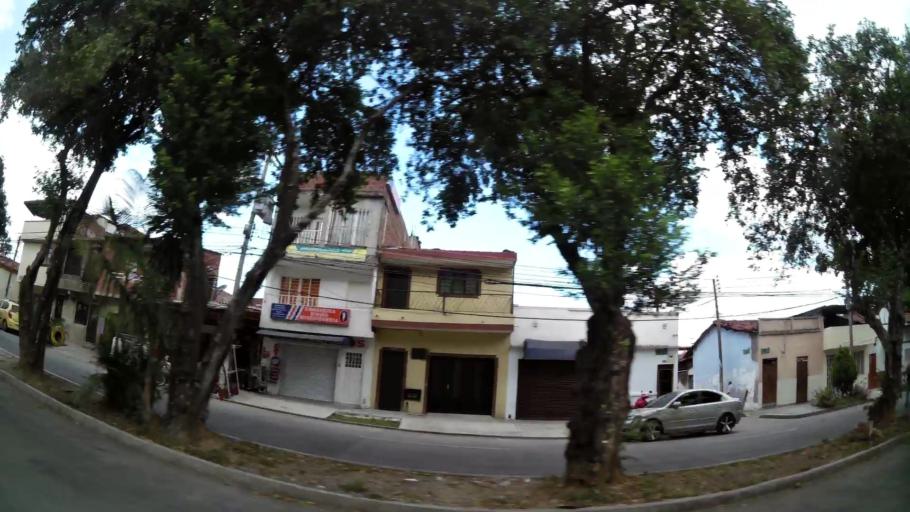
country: CO
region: Valle del Cauca
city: Cali
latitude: 3.4388
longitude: -76.5305
